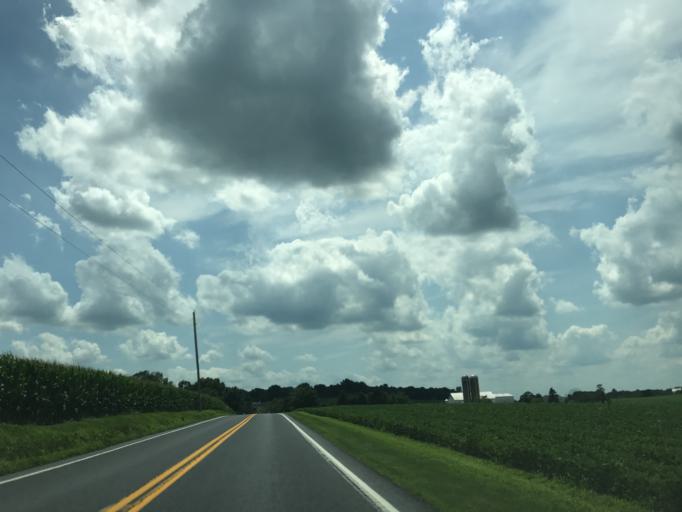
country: US
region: Pennsylvania
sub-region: Lancaster County
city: Manheim
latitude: 40.1975
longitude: -76.4500
